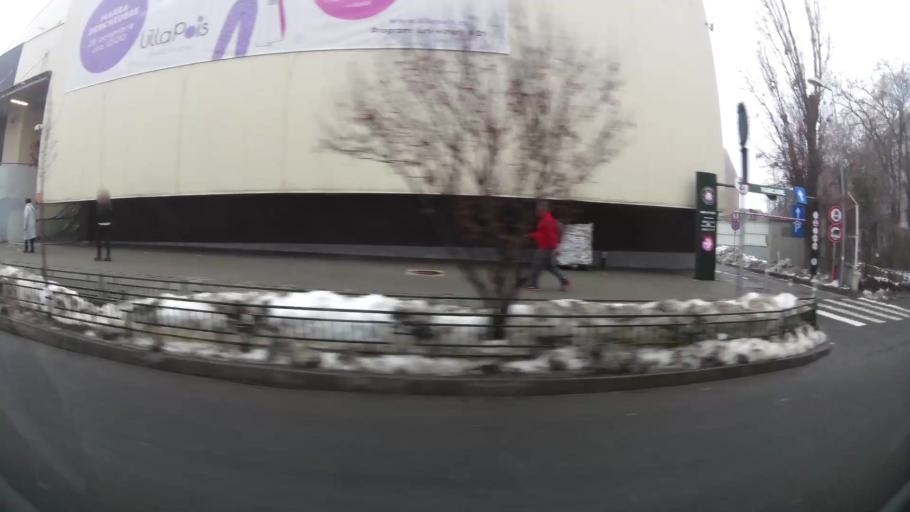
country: RO
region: Ilfov
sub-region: Comuna Chiajna
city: Rosu
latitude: 44.4583
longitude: 26.0407
